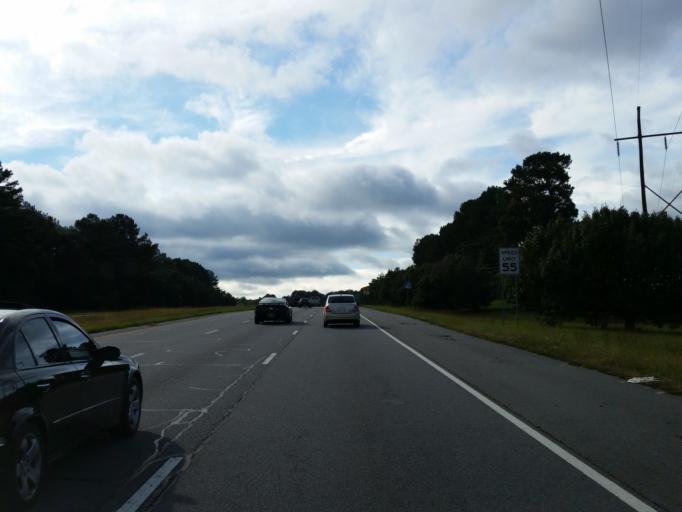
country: US
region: Georgia
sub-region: Cobb County
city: Smyrna
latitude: 33.9229
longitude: -84.4966
